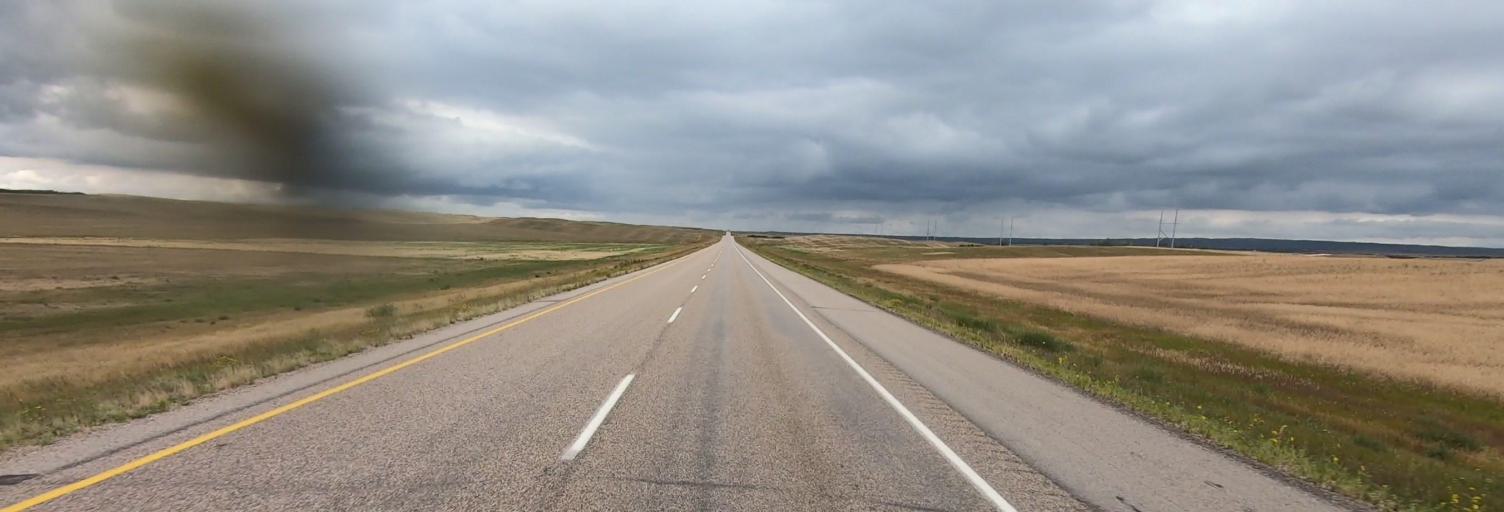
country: CA
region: Saskatchewan
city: Gravelbourg
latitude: 50.4631
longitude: -106.2655
